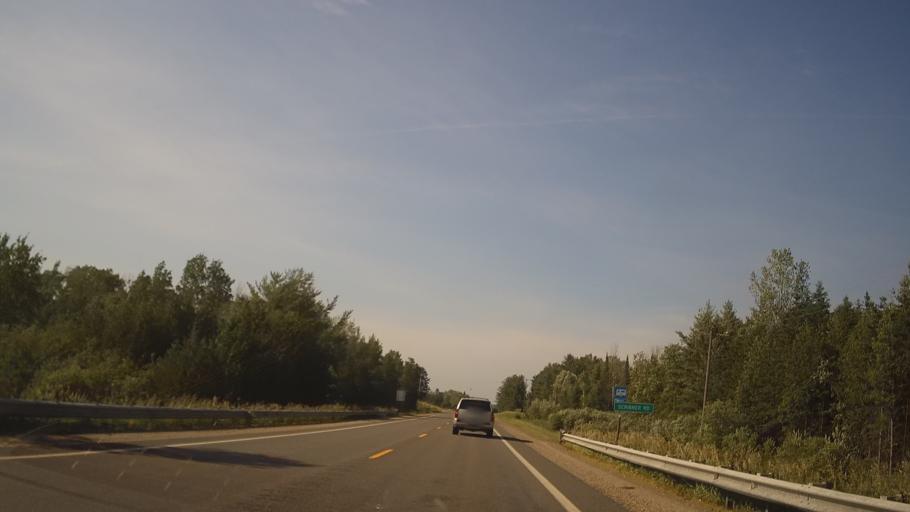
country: US
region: Michigan
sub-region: Ogemaw County
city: West Branch
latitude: 44.3904
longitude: -84.1163
